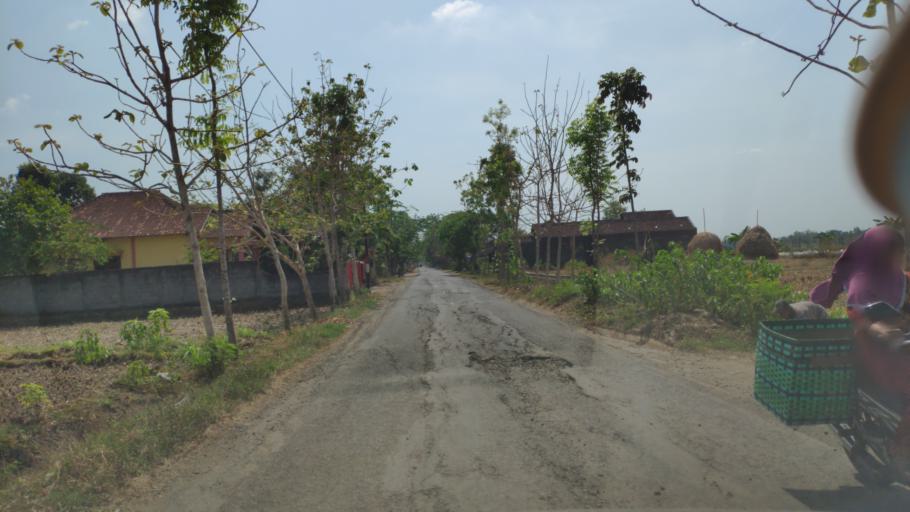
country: ID
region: Central Java
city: Kedungjenar
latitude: -6.9806
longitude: 111.4285
